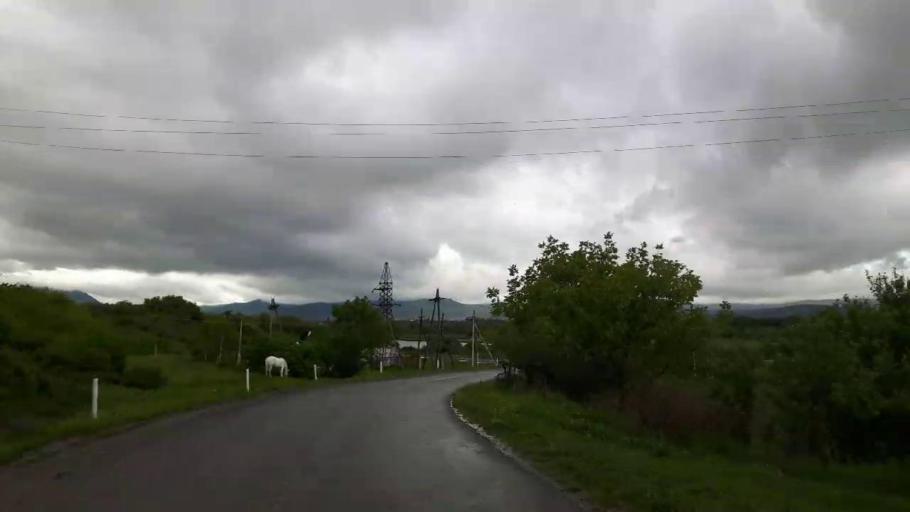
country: GE
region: Shida Kartli
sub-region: Khashuris Raioni
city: Khashuri
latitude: 41.9885
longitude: 43.6608
